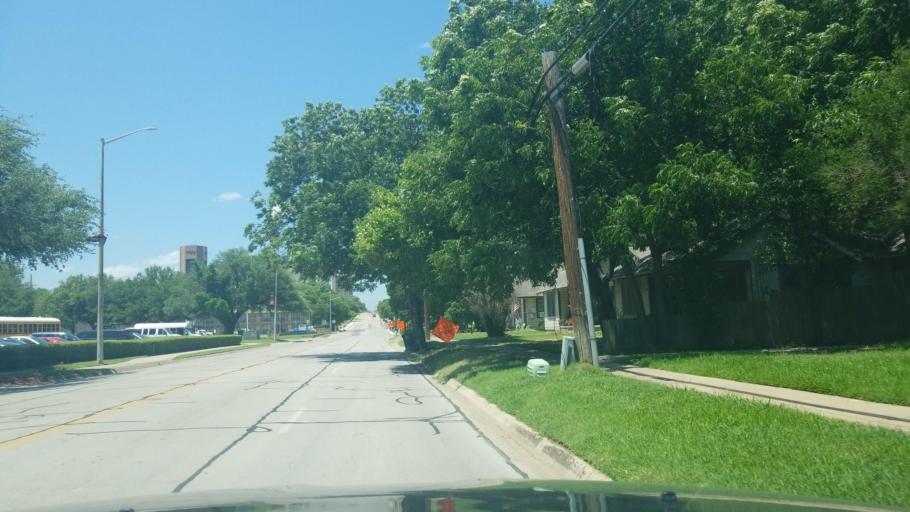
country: US
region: Texas
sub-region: Denton County
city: Denton
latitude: 33.2199
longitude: -97.1273
